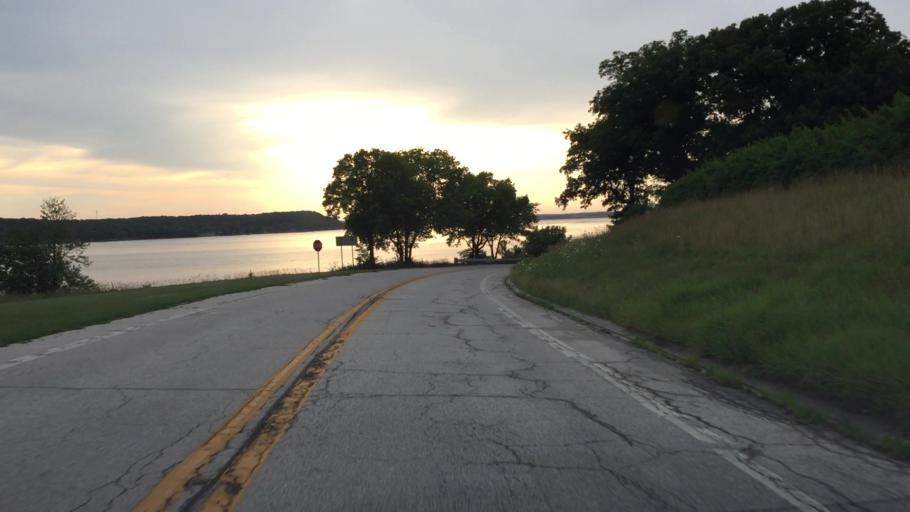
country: US
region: Illinois
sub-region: Hancock County
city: Nauvoo
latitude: 40.5198
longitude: -91.3626
